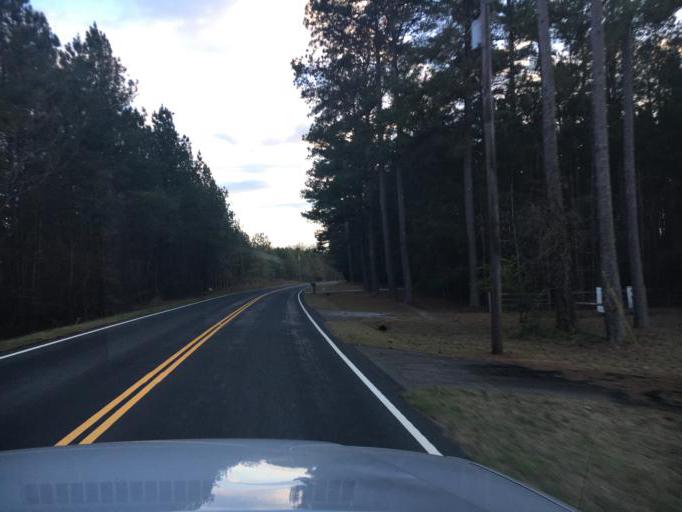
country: US
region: South Carolina
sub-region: Greenwood County
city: Greenwood
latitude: 34.0969
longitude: -82.1883
